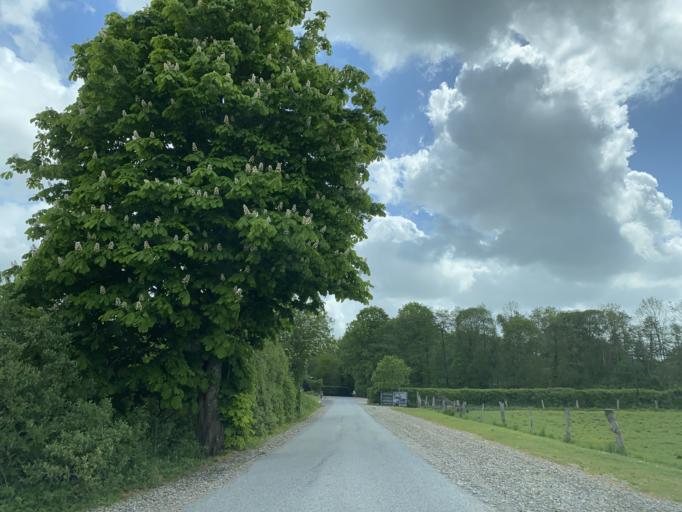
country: DK
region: South Denmark
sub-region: Aabenraa Kommune
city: Lojt Kirkeby
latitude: 55.0101
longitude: 9.4885
